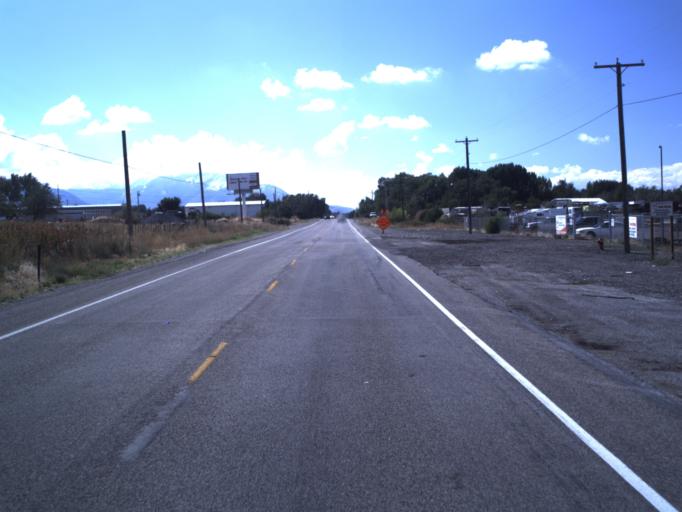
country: US
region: Utah
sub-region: Utah County
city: Springville
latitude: 40.1376
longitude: -111.6162
